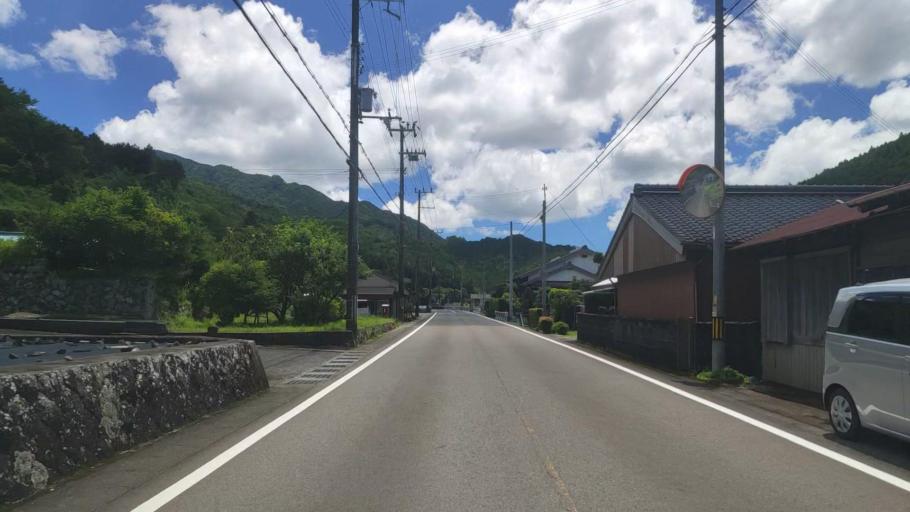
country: JP
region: Mie
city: Owase
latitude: 33.9760
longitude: 136.0549
